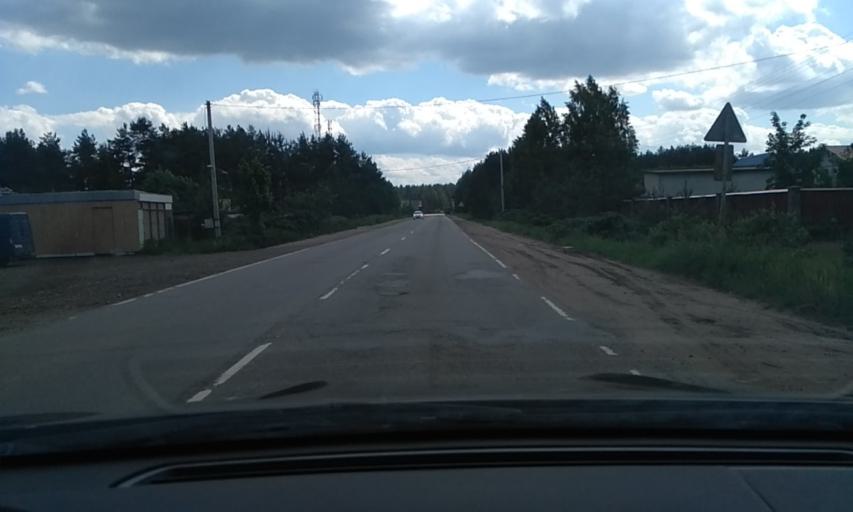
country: RU
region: Leningrad
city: Imeni Sverdlova
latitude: 59.8626
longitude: 30.6712
